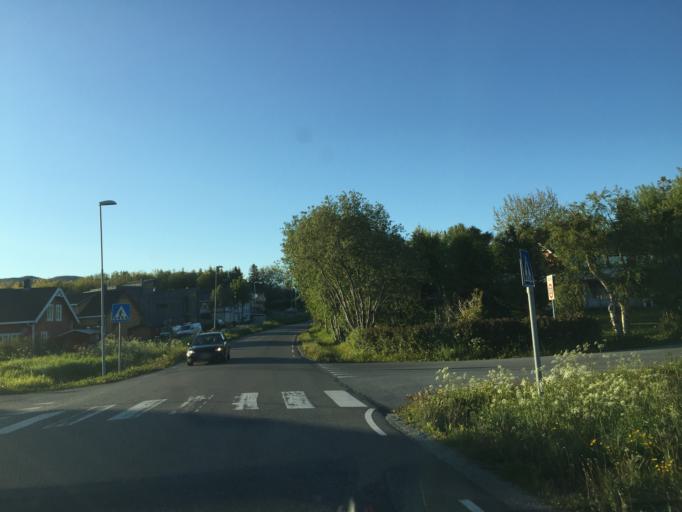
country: NO
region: Nordland
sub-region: Bodo
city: Loding
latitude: 67.2898
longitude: 14.7261
